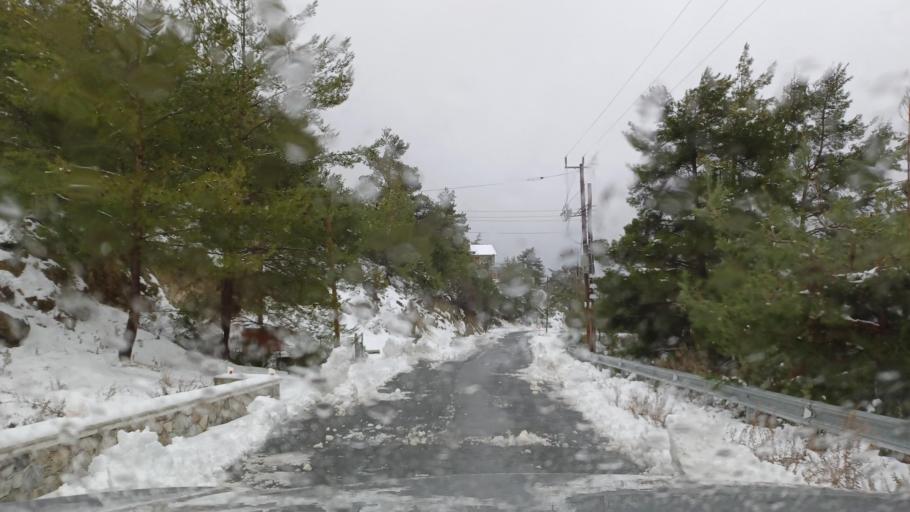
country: CY
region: Limassol
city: Pelendri
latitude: 34.9081
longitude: 32.9593
